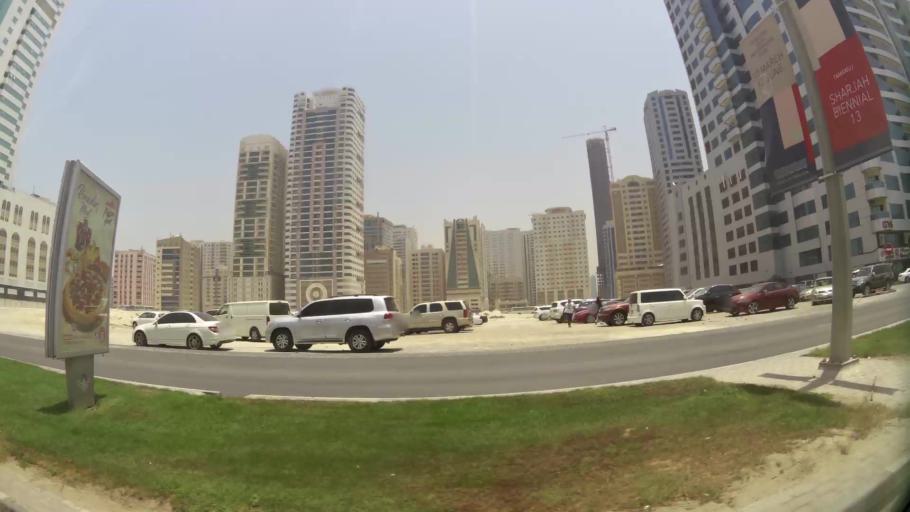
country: AE
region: Ash Shariqah
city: Sharjah
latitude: 25.3254
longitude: 55.3728
